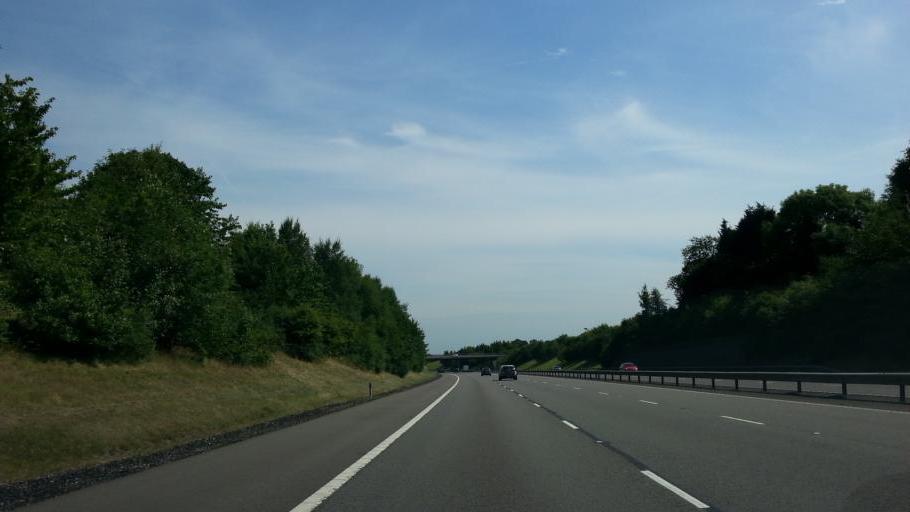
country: GB
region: England
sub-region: City and Borough of Birmingham
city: Sutton Coldfield
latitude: 52.5886
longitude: -1.7935
